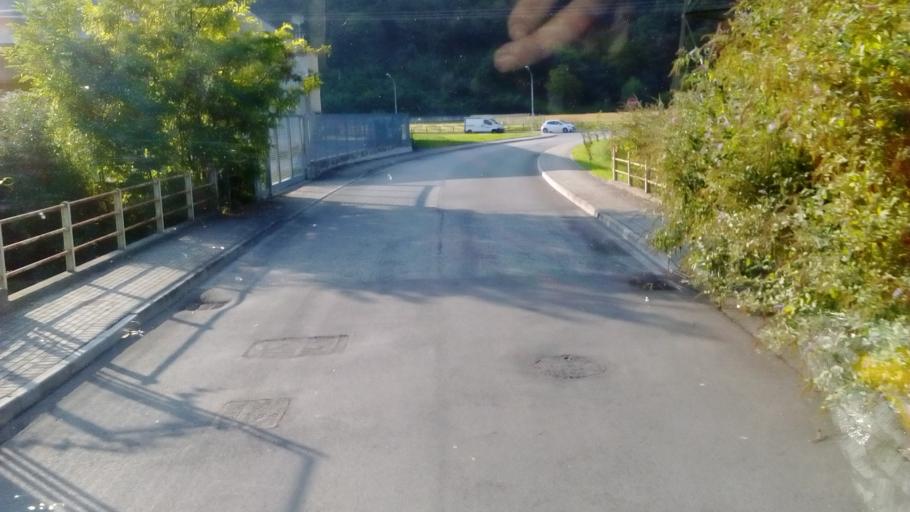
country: IT
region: Lombardy
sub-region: Provincia di Sondrio
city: Morbegno
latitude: 46.1352
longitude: 9.5884
